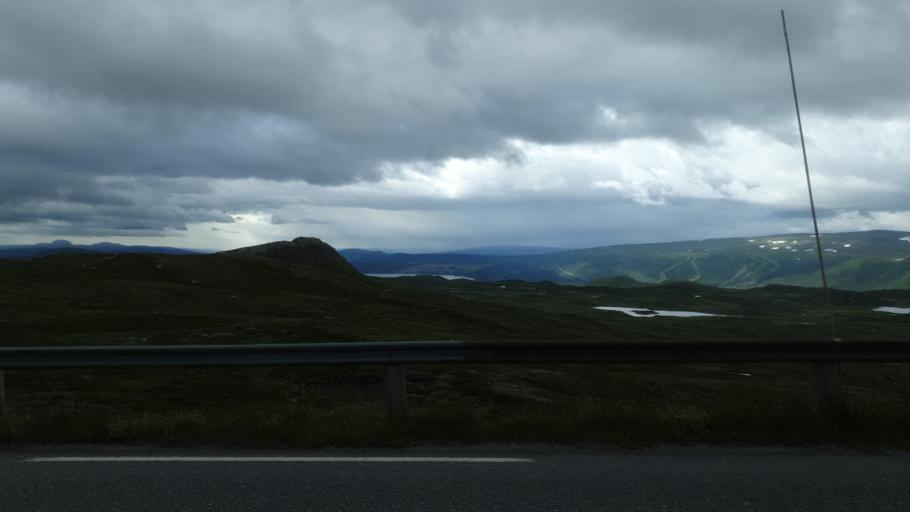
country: NO
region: Oppland
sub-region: Vestre Slidre
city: Slidre
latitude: 61.2867
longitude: 8.8207
